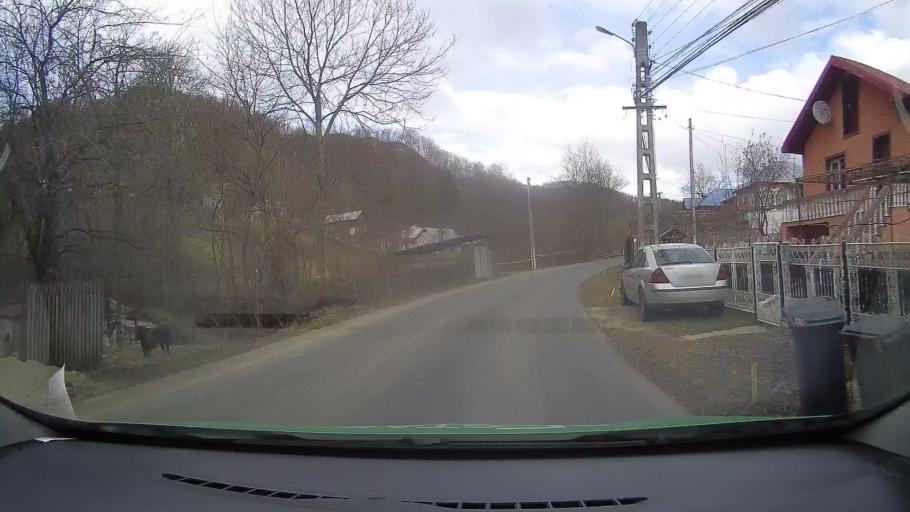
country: RO
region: Dambovita
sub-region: Comuna Visinesti
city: Visinesti
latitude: 45.1068
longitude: 25.5532
